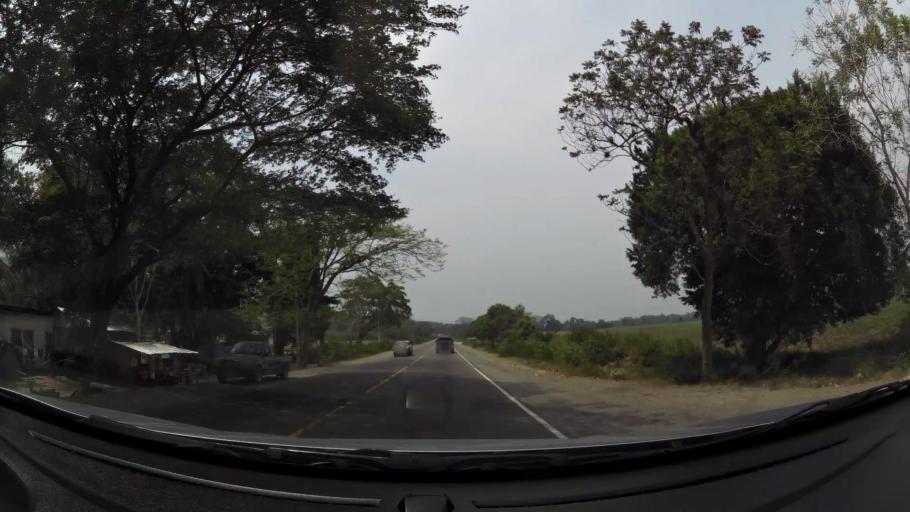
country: HN
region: Cortes
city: Potrerillos
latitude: 15.1875
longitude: -87.9616
